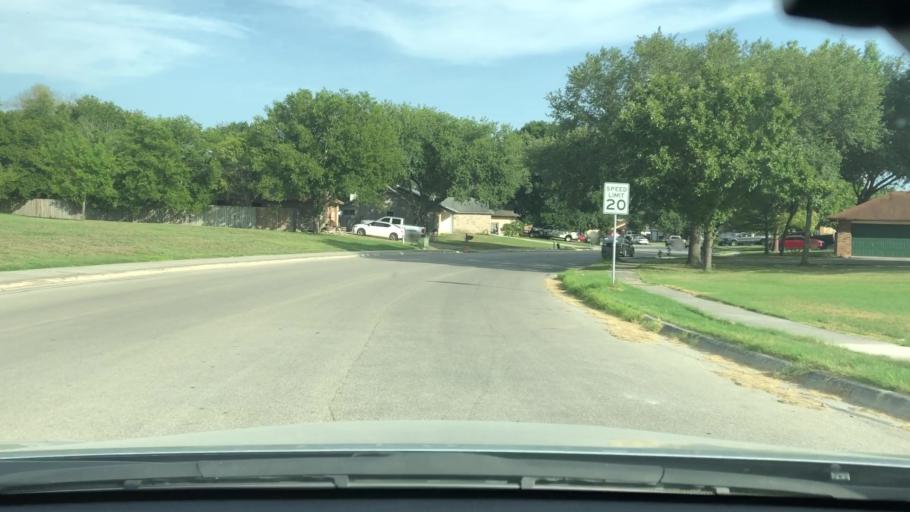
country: US
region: Texas
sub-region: Bexar County
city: Converse
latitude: 29.5384
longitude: -98.3269
